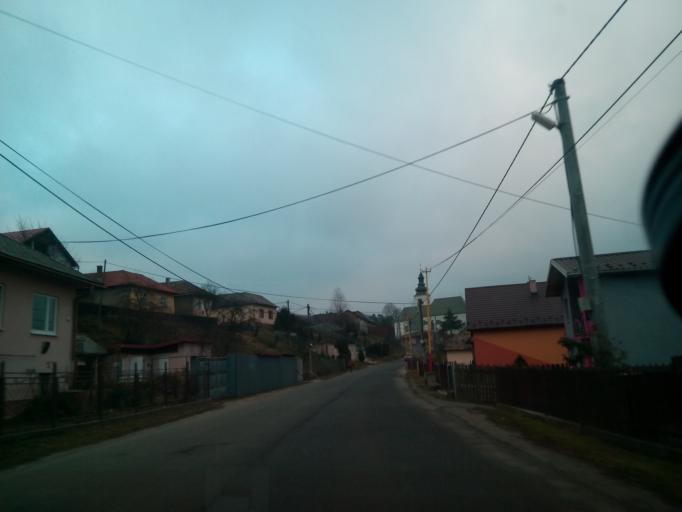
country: SK
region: Kosicky
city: Krompachy
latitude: 48.9229
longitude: 20.9352
